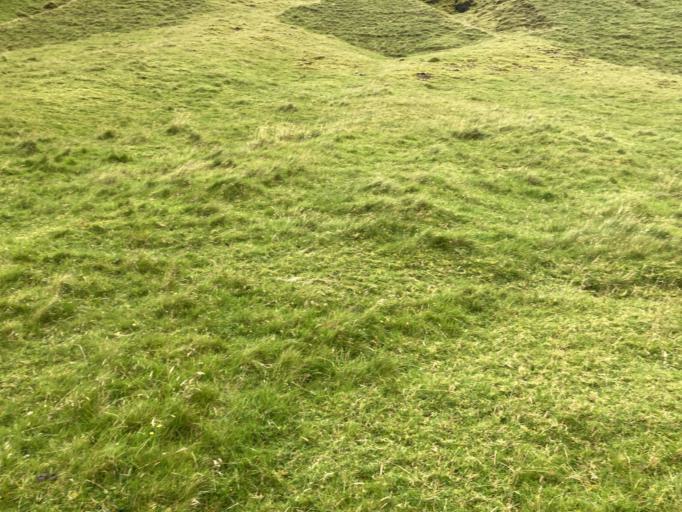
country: GB
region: Scotland
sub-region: Highland
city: Isle of Skye
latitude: 57.0164
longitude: -6.3890
